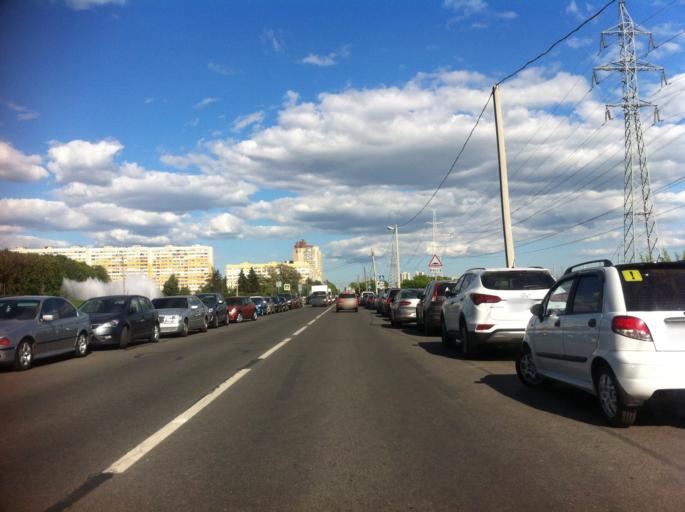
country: RU
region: St.-Petersburg
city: Uritsk
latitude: 59.8473
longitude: 30.1696
